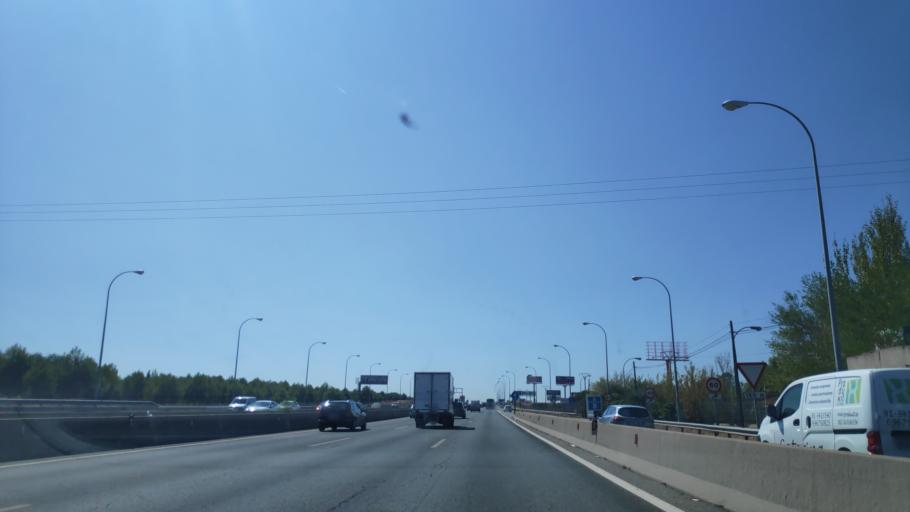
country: ES
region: Madrid
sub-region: Provincia de Madrid
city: Villaverde
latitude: 40.3607
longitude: -3.7214
